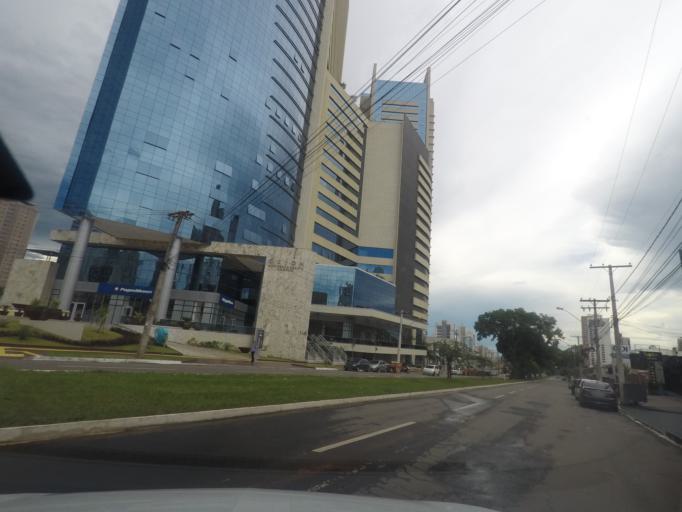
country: BR
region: Goias
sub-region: Goiania
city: Goiania
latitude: -16.6973
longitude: -49.2692
